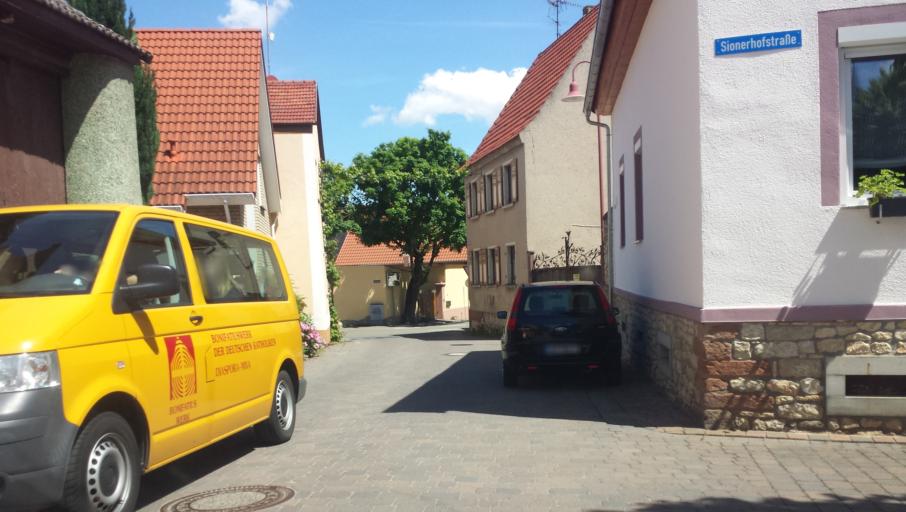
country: DE
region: Rheinland-Pfalz
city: Gundersheim
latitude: 49.6952
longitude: 8.2032
